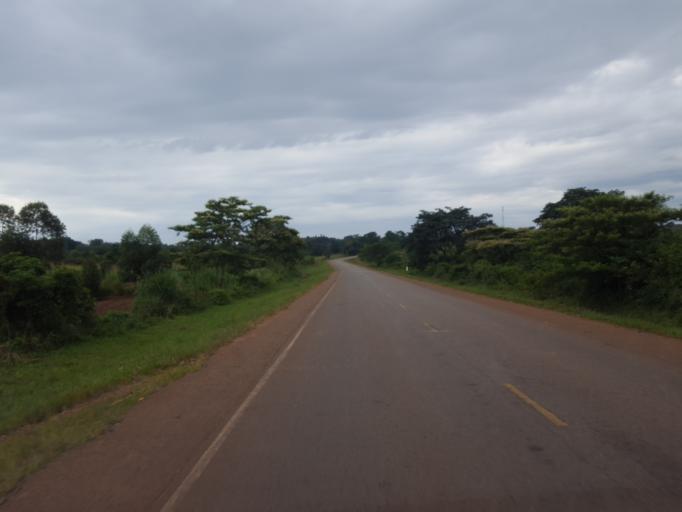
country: UG
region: Central Region
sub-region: Kiboga District
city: Kiboga
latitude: 1.0198
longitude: 31.6872
